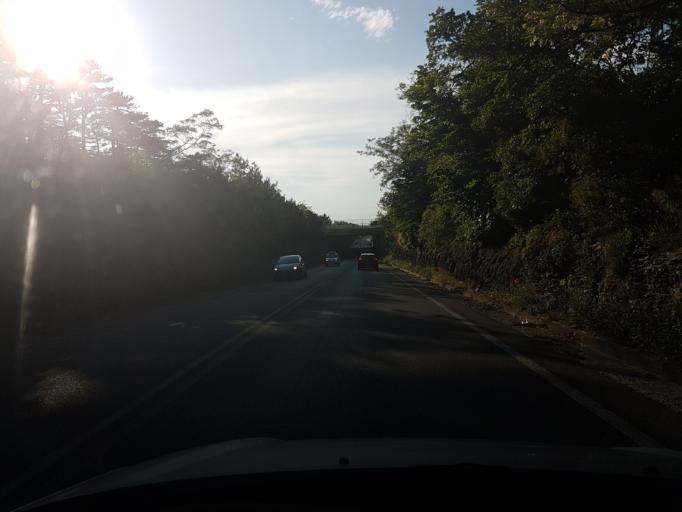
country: IT
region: Friuli Venezia Giulia
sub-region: Provincia di Trieste
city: Prosecco-Contovello
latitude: 45.7020
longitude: 13.7546
